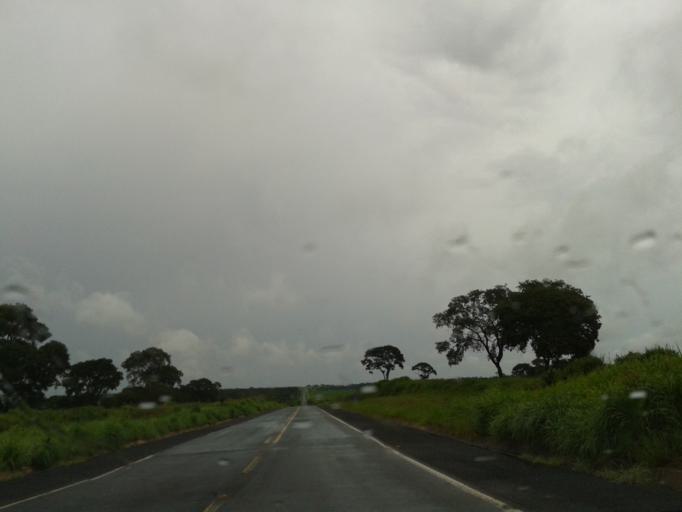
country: BR
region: Minas Gerais
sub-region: Santa Vitoria
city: Santa Vitoria
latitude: -19.1522
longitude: -50.1459
